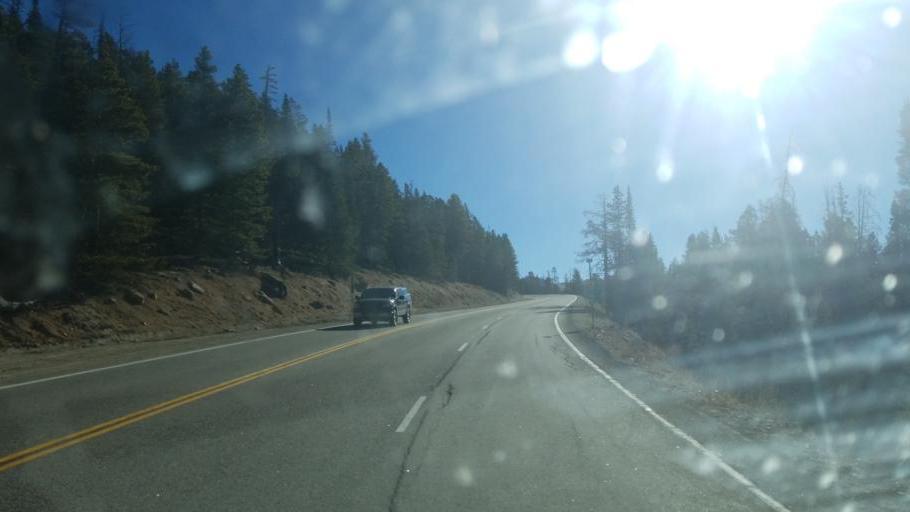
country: US
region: Colorado
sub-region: Chaffee County
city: Salida
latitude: 38.4855
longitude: -106.3365
